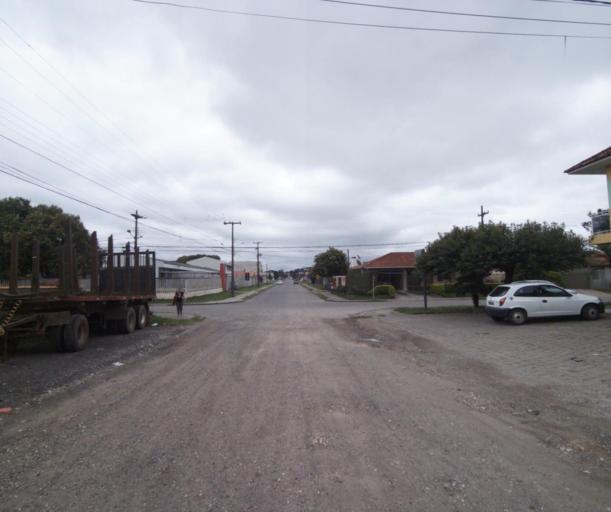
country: BR
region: Parana
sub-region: Quatro Barras
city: Quatro Barras
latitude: -25.3618
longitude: -49.0984
